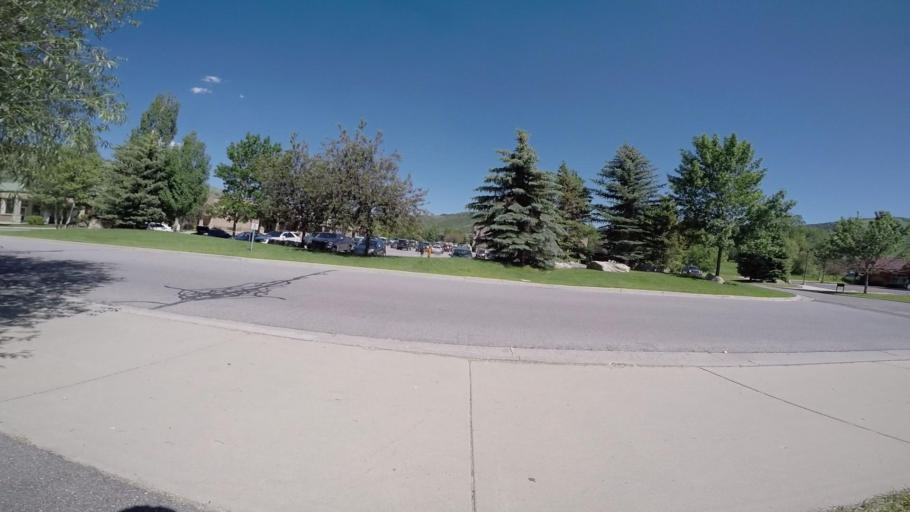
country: US
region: Utah
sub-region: Summit County
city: Park City
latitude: 40.6623
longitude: -111.5107
